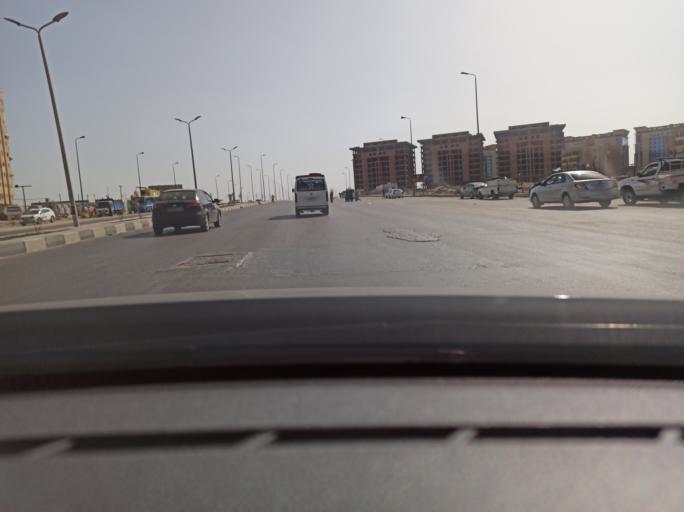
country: EG
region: Muhafazat al Qahirah
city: Cairo
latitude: 30.0513
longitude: 31.3998
